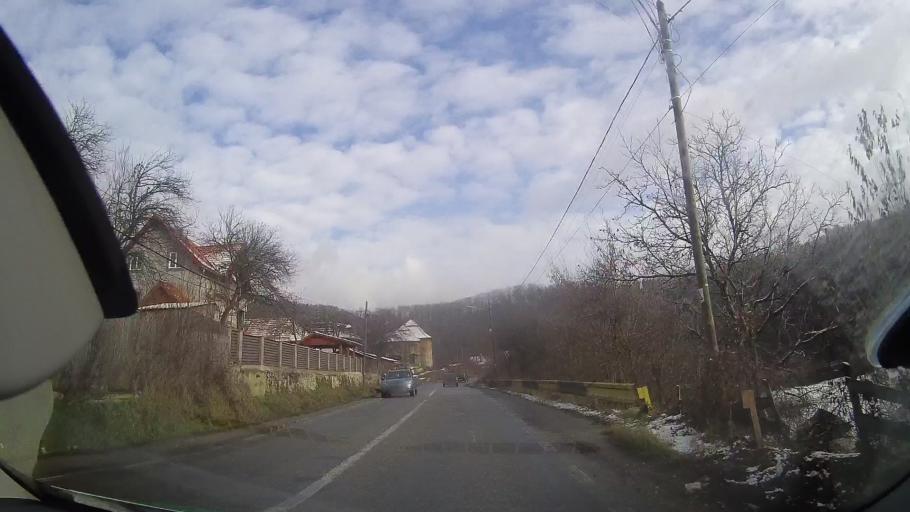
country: RO
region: Alba
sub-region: Oras Baia de Aries
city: Baia de Aries
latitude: 46.3758
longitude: 23.2593
